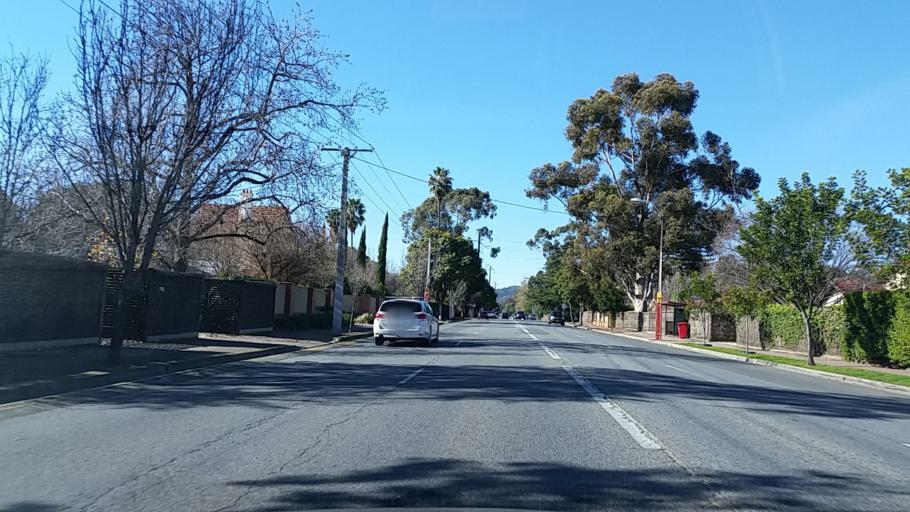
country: AU
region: South Australia
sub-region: Norwood Payneham St Peters
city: Trinity Gardens
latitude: -34.9273
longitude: 138.6355
